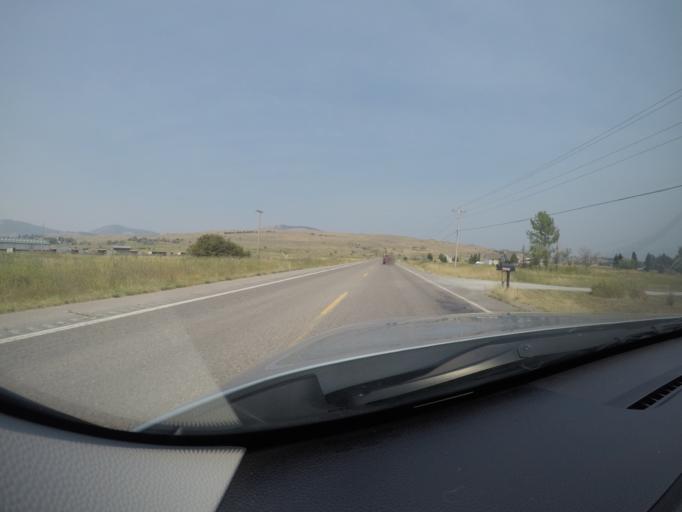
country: US
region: Montana
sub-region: Lake County
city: Polson
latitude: 47.7289
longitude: -114.1886
